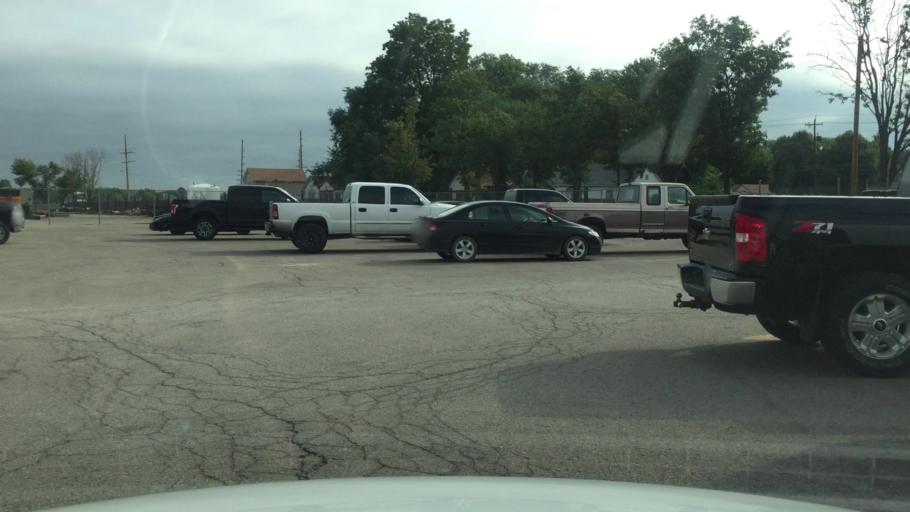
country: US
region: Kansas
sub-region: Shawnee County
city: Topeka
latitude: 39.0601
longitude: -95.6561
